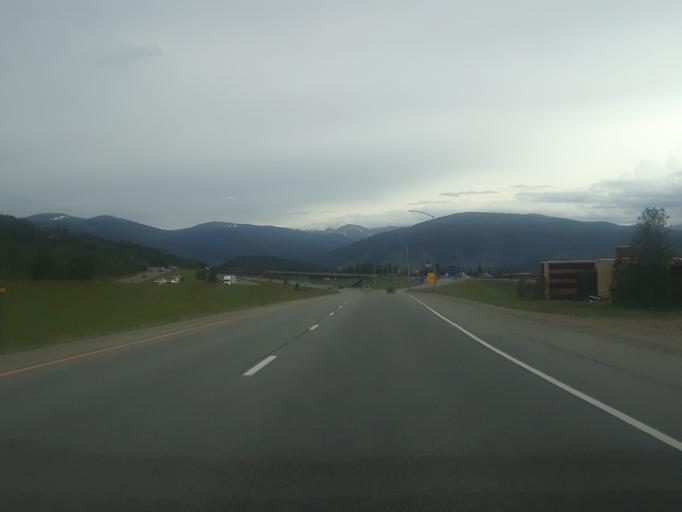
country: US
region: Colorado
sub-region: Summit County
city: Frisco
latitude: 39.5899
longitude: -106.1004
